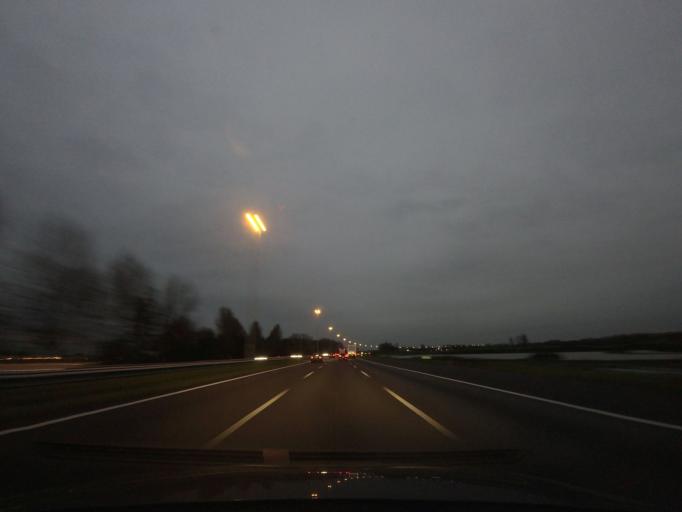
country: NL
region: Utrecht
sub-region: Gemeente Vianen
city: Vianen
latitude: 51.9622
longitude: 5.0853
